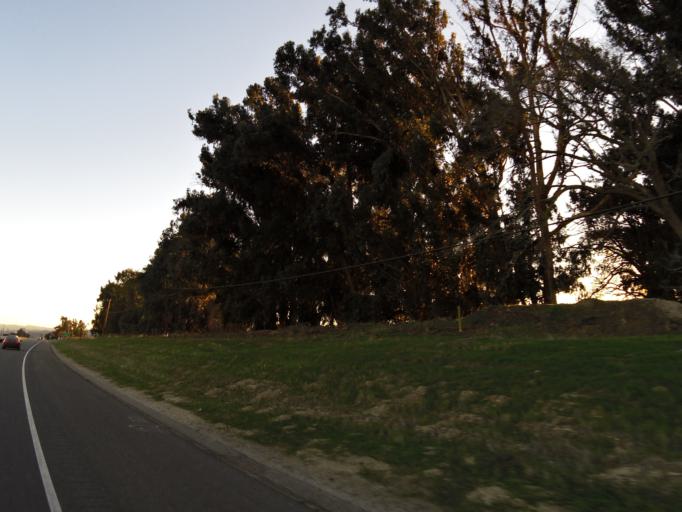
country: US
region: California
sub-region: Monterey County
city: King City
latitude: 36.2690
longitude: -121.1812
